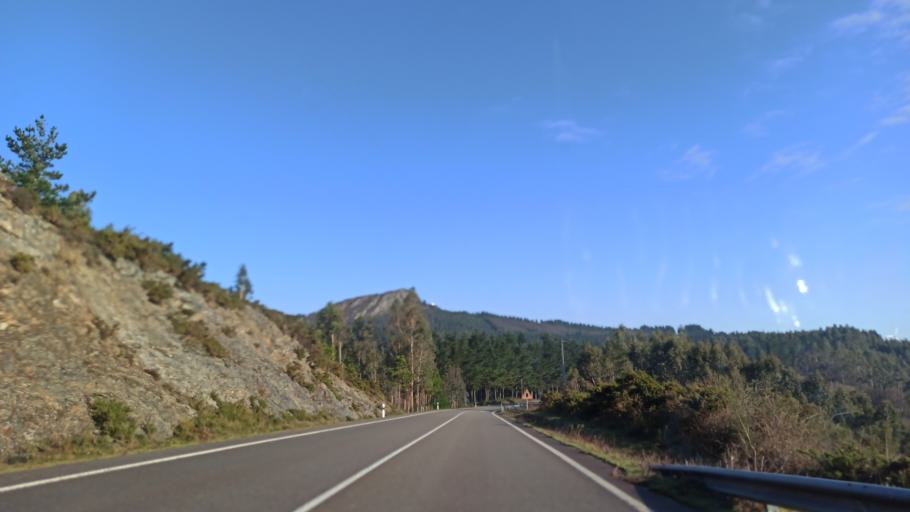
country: ES
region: Galicia
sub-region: Provincia da Coruna
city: As Pontes de Garcia Rodriguez
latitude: 43.4994
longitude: -7.8298
